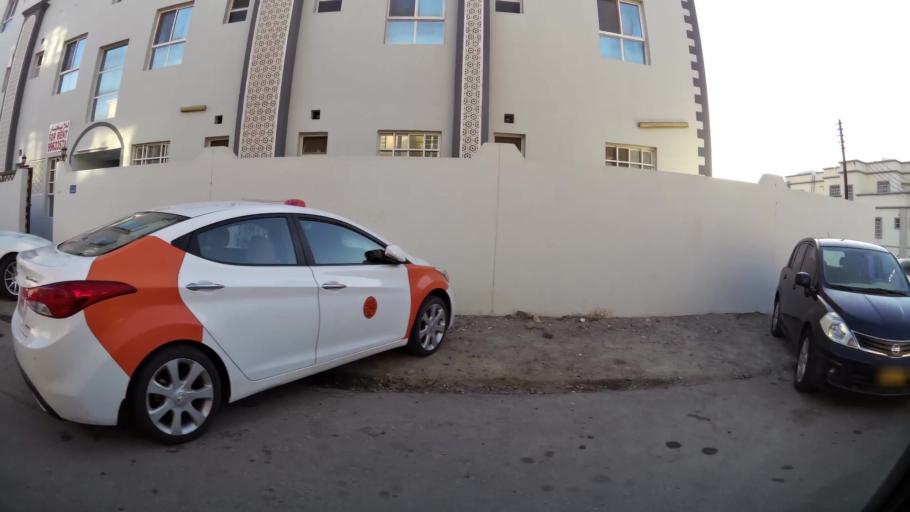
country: OM
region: Muhafazat Masqat
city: Muscat
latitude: 23.5673
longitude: 58.5804
